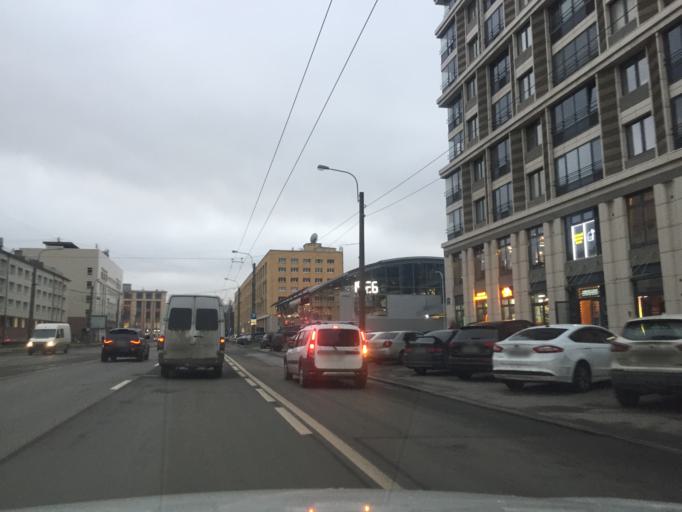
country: RU
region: St.-Petersburg
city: Petrogradka
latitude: 59.9736
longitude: 30.3160
